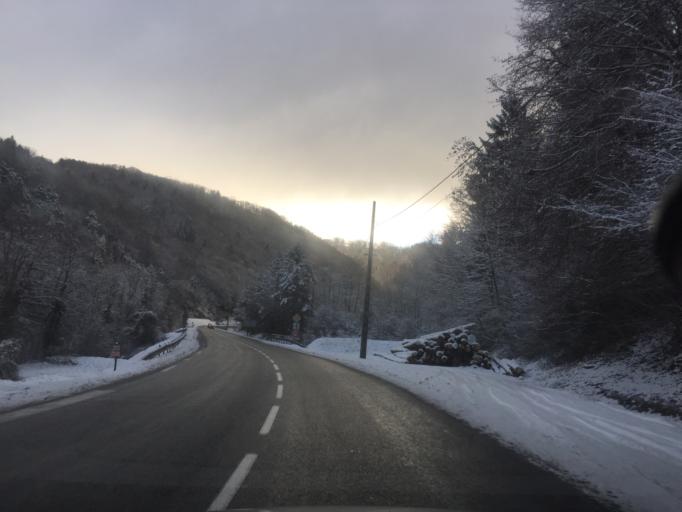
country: FR
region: Rhone-Alpes
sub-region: Departement de la Haute-Savoie
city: Armoy
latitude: 46.3643
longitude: 6.5121
